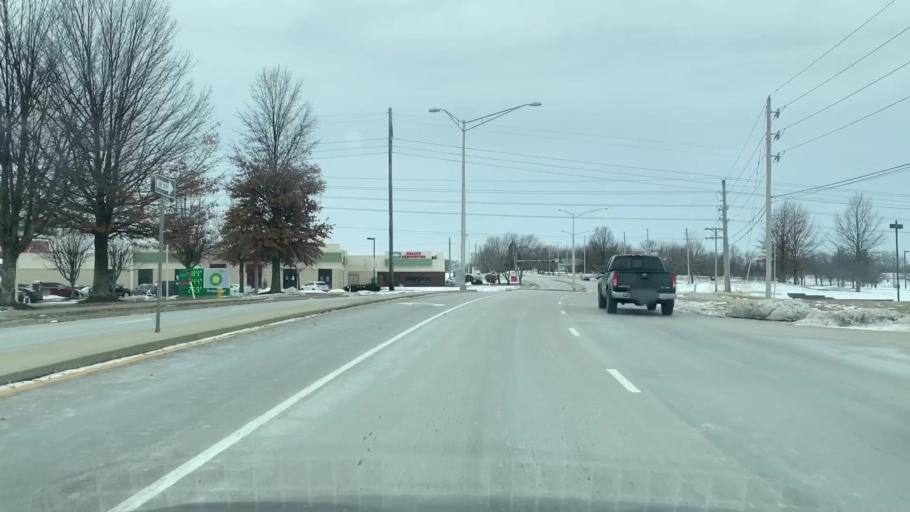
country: US
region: Missouri
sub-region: Jackson County
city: Lees Summit
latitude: 38.9328
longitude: -94.3788
